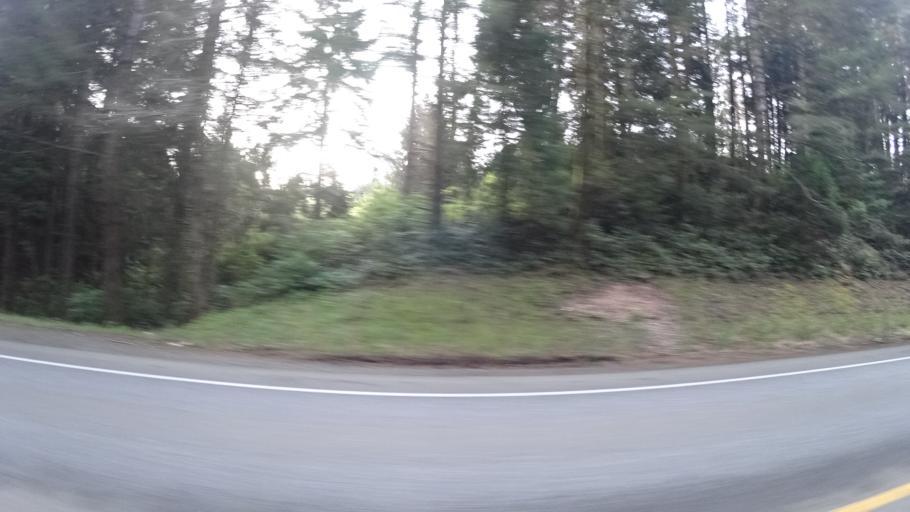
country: US
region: Oregon
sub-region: Coos County
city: Lakeside
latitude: 43.5467
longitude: -124.2115
